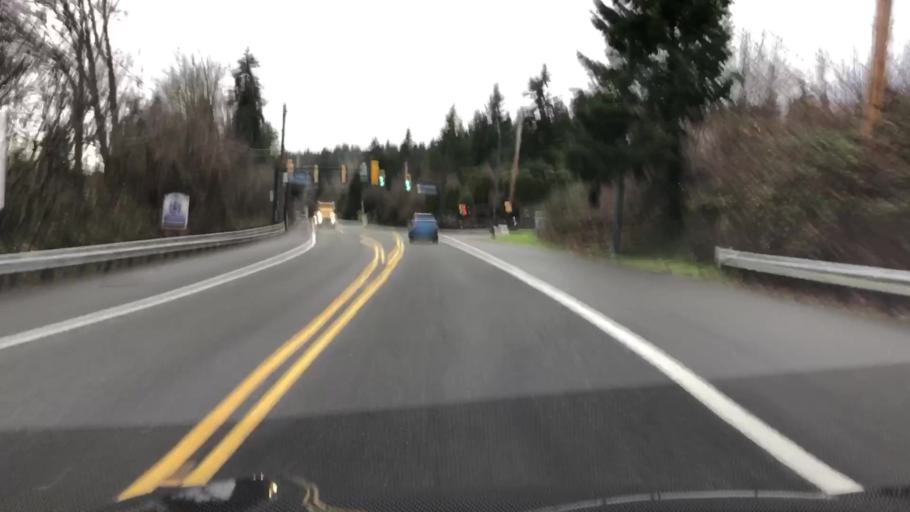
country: US
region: Washington
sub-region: King County
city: City of Sammamish
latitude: 47.6124
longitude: -122.0683
